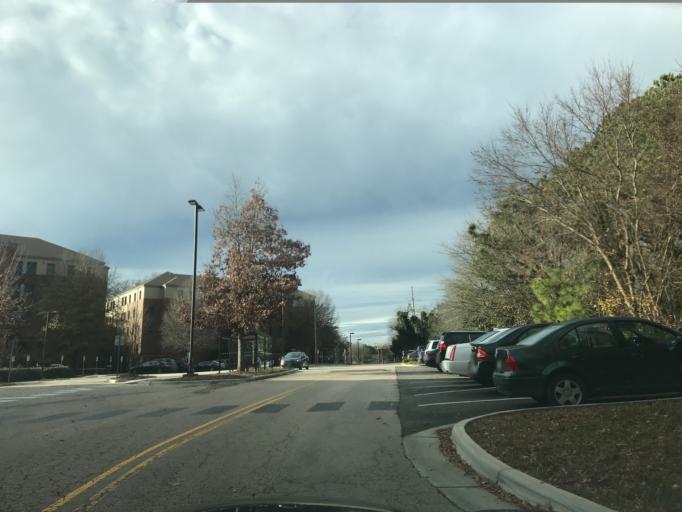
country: US
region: North Carolina
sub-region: Wake County
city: West Raleigh
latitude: 35.7867
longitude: -78.6835
